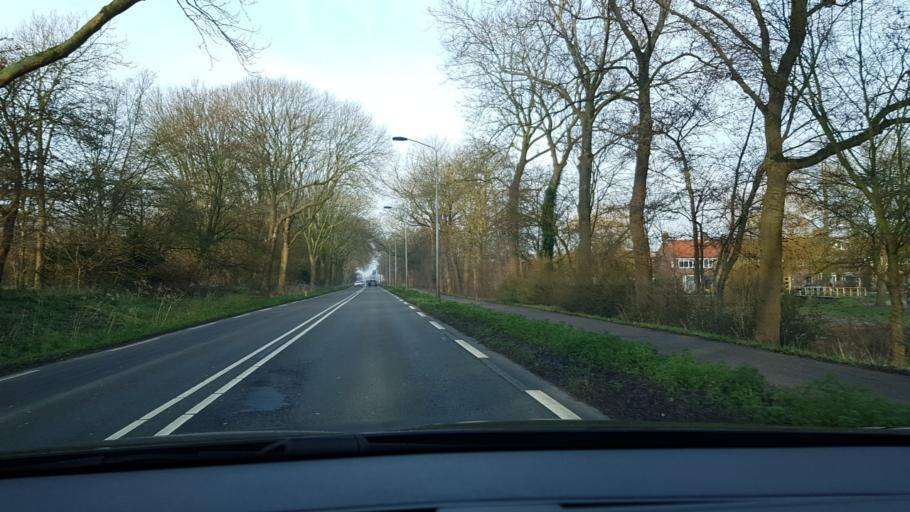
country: NL
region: North Holland
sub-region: Gemeente Uithoorn
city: Uithoorn
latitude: 52.2375
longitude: 4.8225
